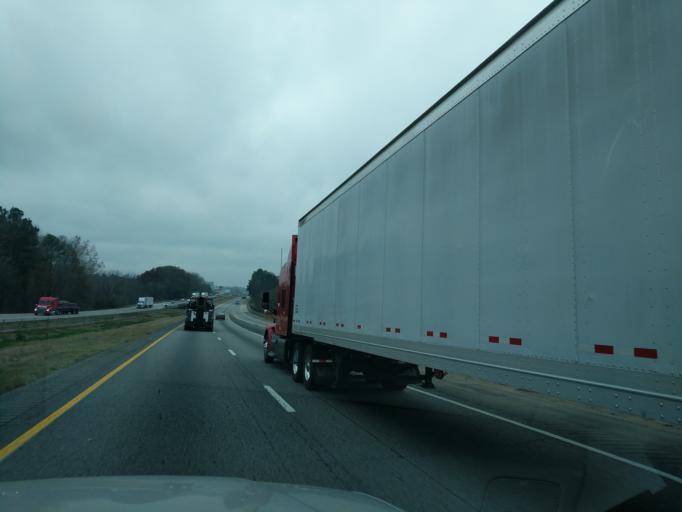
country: US
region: Georgia
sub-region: Jackson County
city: Jefferson
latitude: 34.1523
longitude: -83.6465
